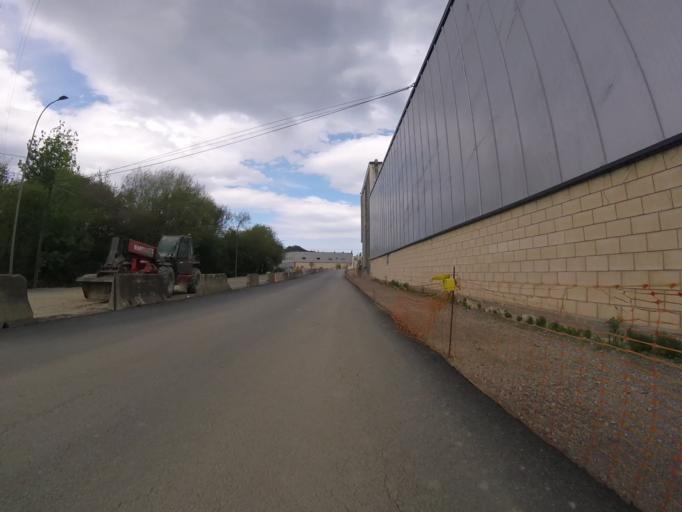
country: ES
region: Basque Country
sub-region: Provincia de Guipuzcoa
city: Zarautz
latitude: 43.2757
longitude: -2.1701
